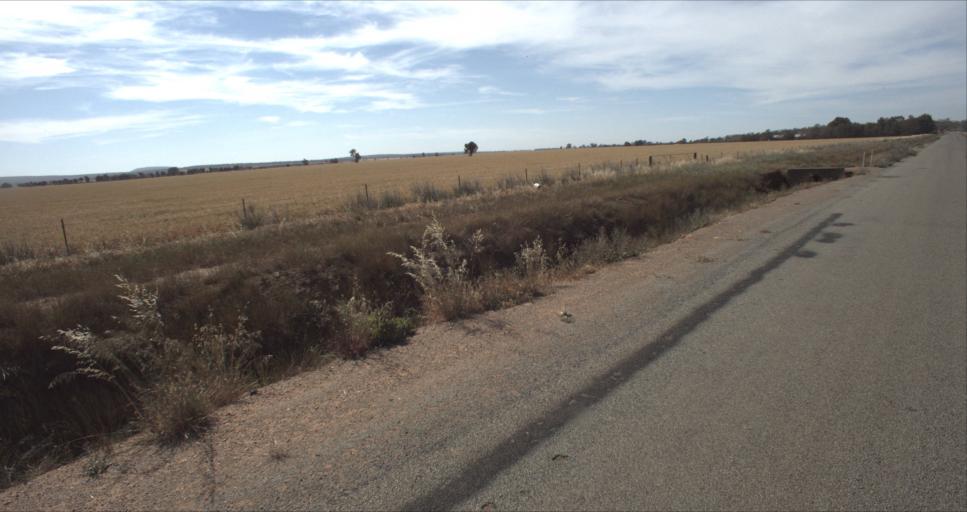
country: AU
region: New South Wales
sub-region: Leeton
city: Leeton
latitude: -34.5670
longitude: 146.4721
